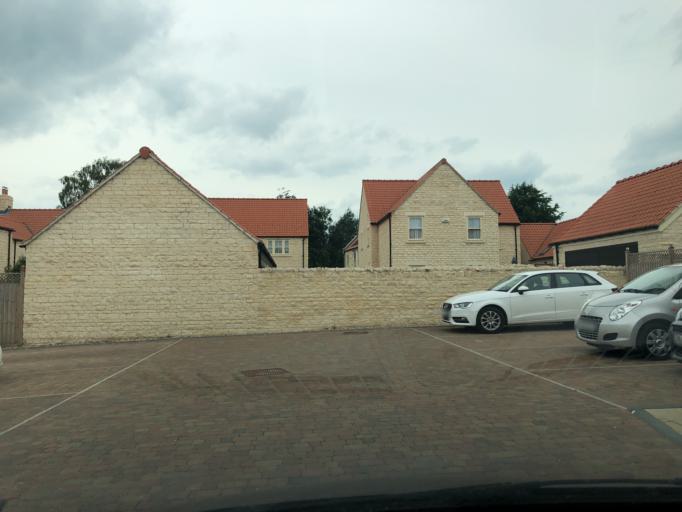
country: GB
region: England
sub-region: North Yorkshire
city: Helmsley
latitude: 54.2478
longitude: -1.0538
